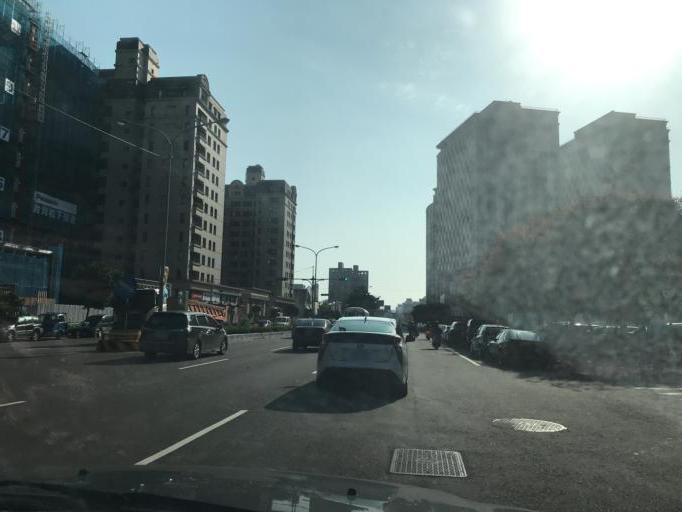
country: TW
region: Taiwan
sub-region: Hsinchu
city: Zhubei
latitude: 24.8223
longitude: 121.0301
